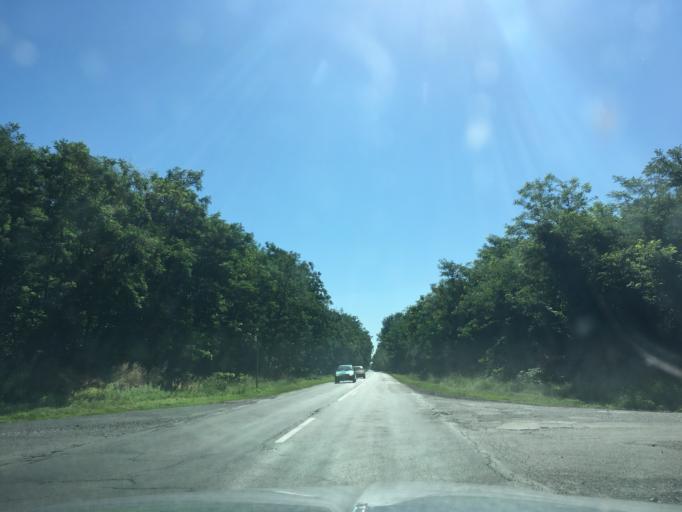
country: HU
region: Hajdu-Bihar
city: Hajdusamson
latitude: 47.5274
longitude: 21.7340
